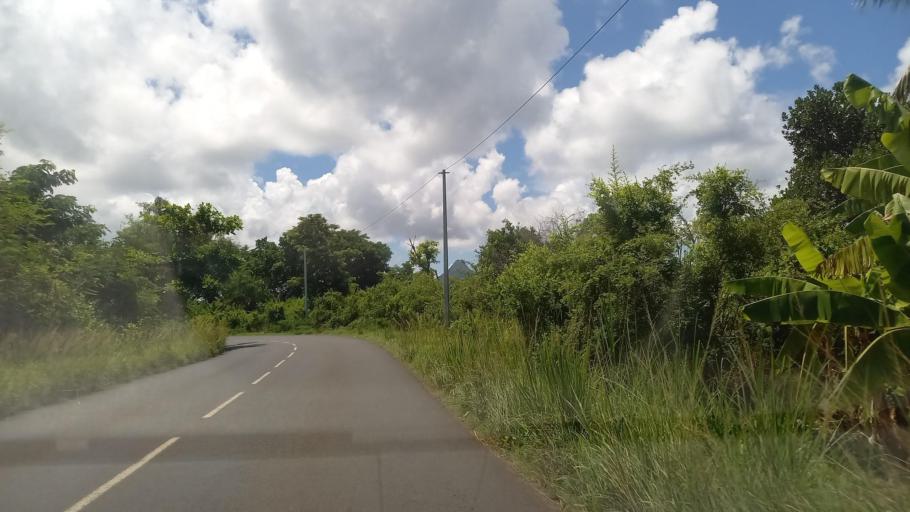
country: YT
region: Ouangani
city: Ouangani
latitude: -12.8808
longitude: 45.1254
